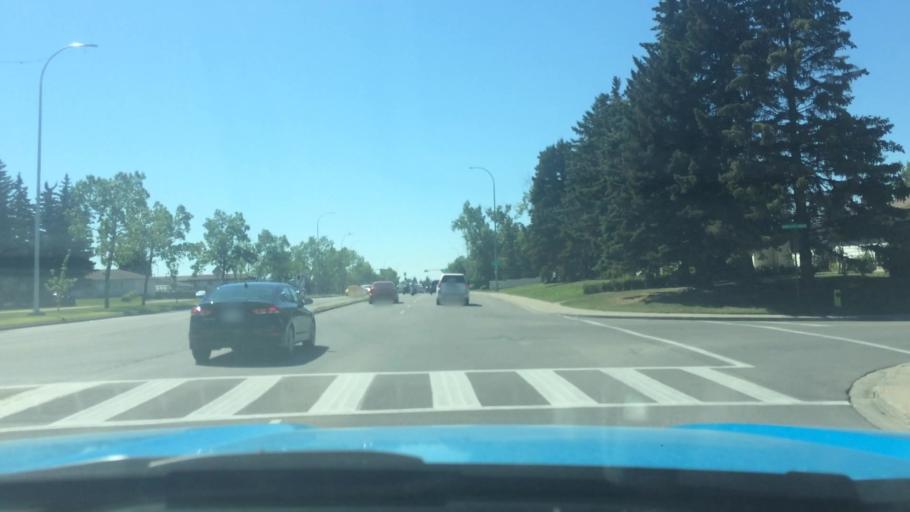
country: CA
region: Alberta
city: Calgary
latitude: 51.0571
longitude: -113.9575
